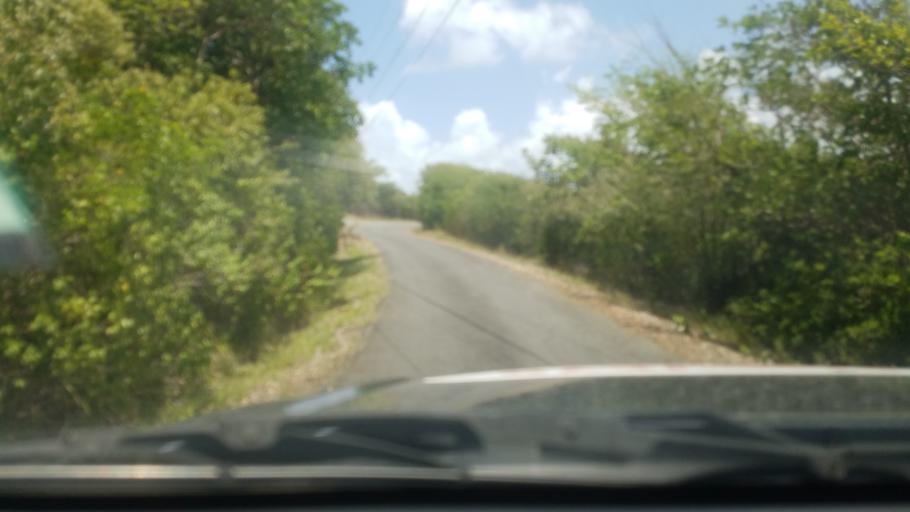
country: LC
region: Vieux-Fort
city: Vieux Fort
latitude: 13.7135
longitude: -60.9468
